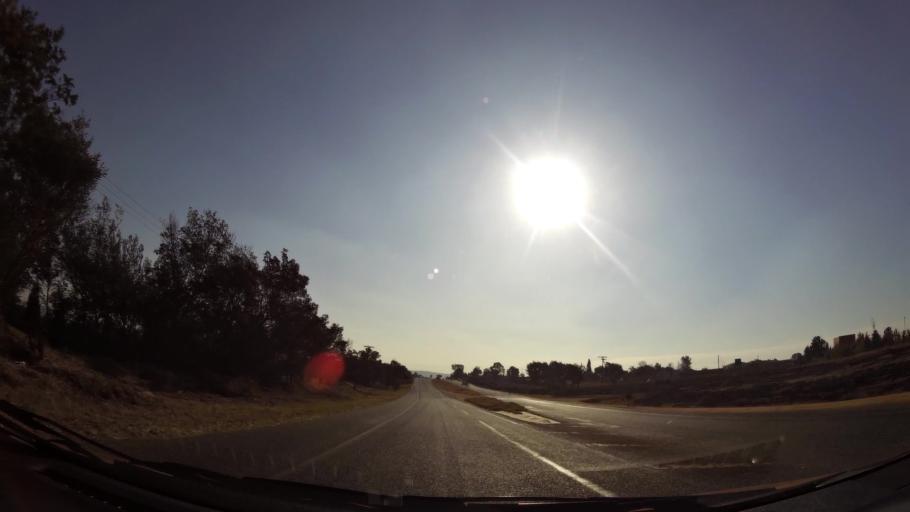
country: ZA
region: Gauteng
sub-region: West Rand District Municipality
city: Muldersdriseloop
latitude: -26.0293
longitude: 27.8713
